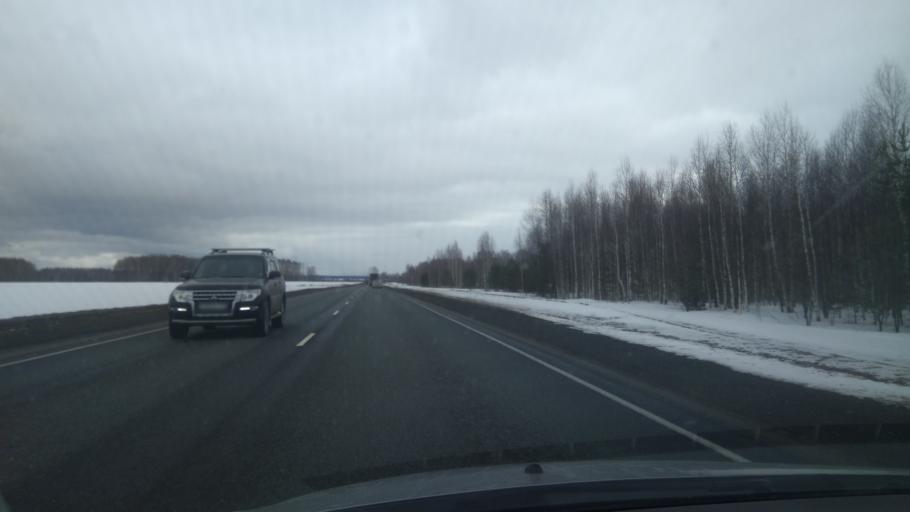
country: RU
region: Perm
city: Suksun
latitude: 56.9829
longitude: 57.5058
